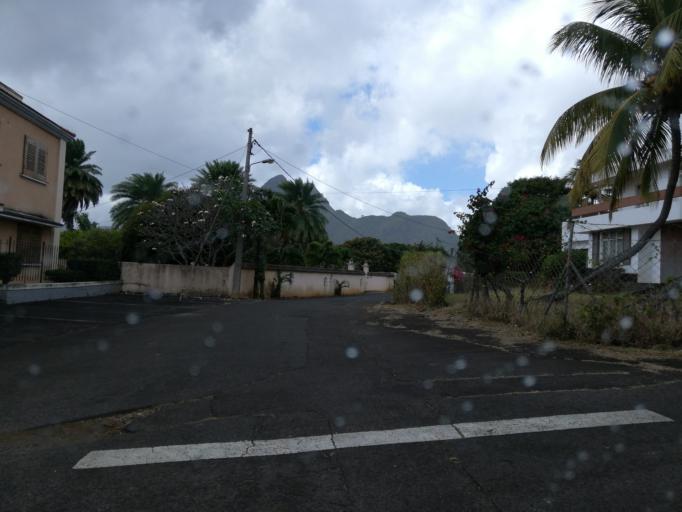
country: MU
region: Moka
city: Pailles
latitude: -20.2105
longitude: 57.4720
